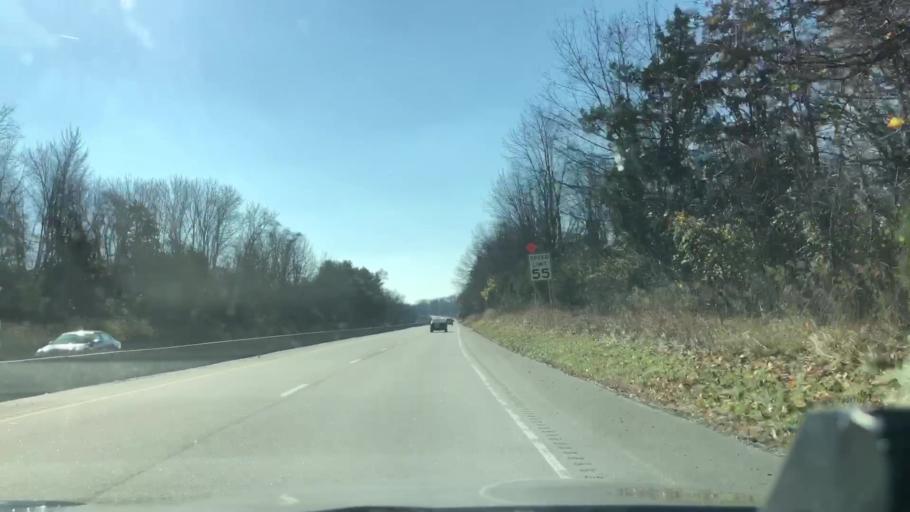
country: US
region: Pennsylvania
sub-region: Montgomery County
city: Halfway House
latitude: 40.2840
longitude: -75.6444
